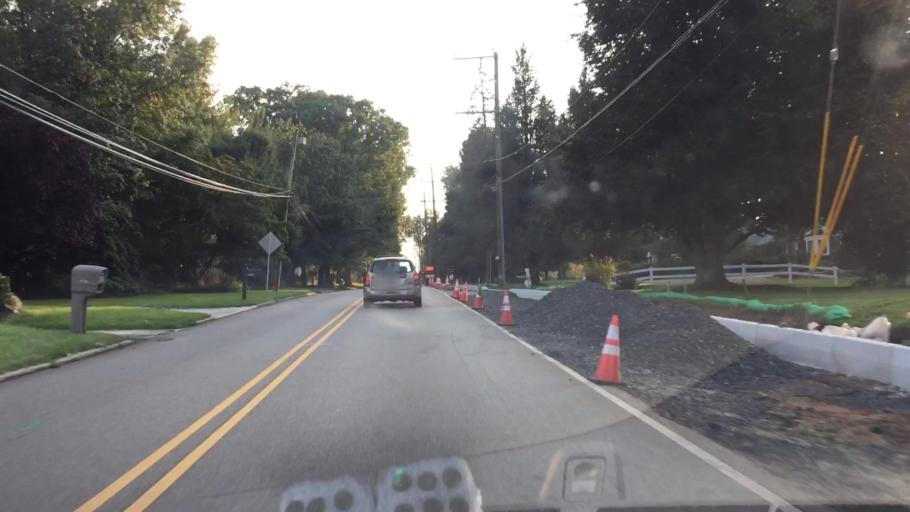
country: US
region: Pennsylvania
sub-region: Montgomery County
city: Blue Bell
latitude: 40.1426
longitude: -75.2987
